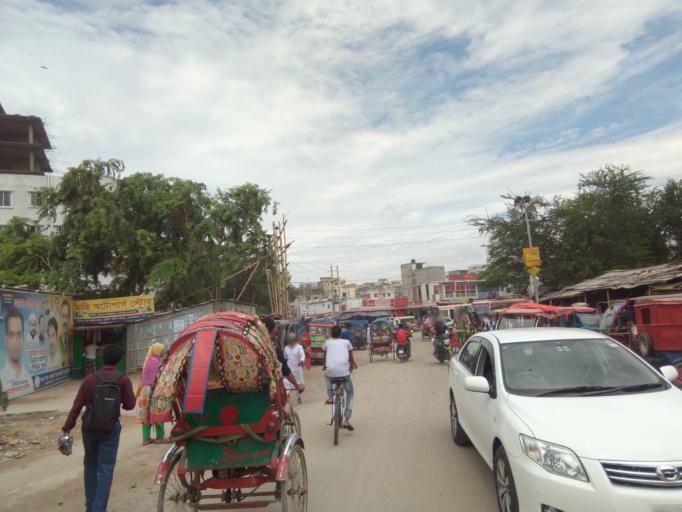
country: BD
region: Dhaka
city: Azimpur
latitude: 23.7568
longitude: 90.3561
